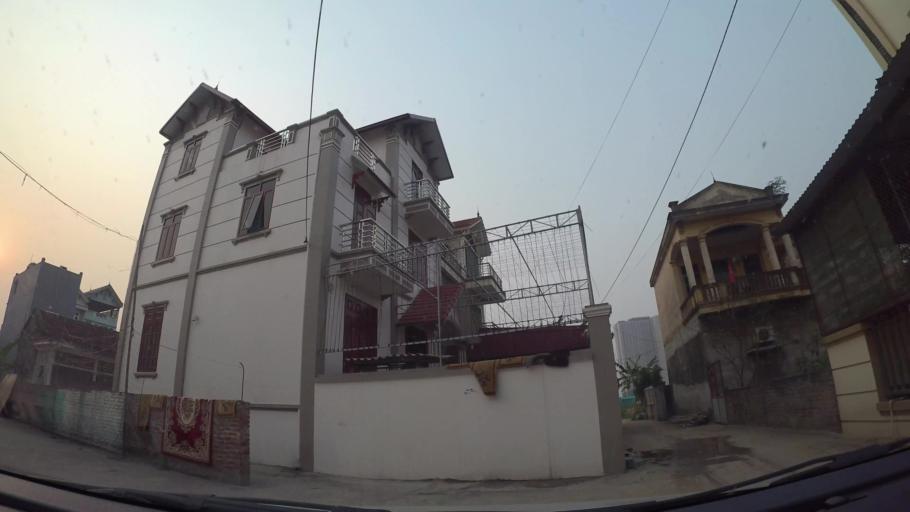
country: VN
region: Ha Noi
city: Cau Dien
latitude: 21.0028
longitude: 105.7295
